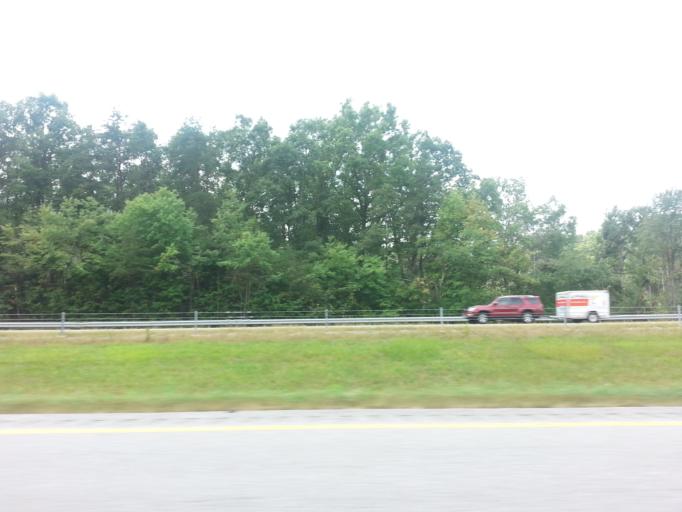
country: US
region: Tennessee
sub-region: Putnam County
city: Monterey
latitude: 36.0729
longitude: -85.1975
